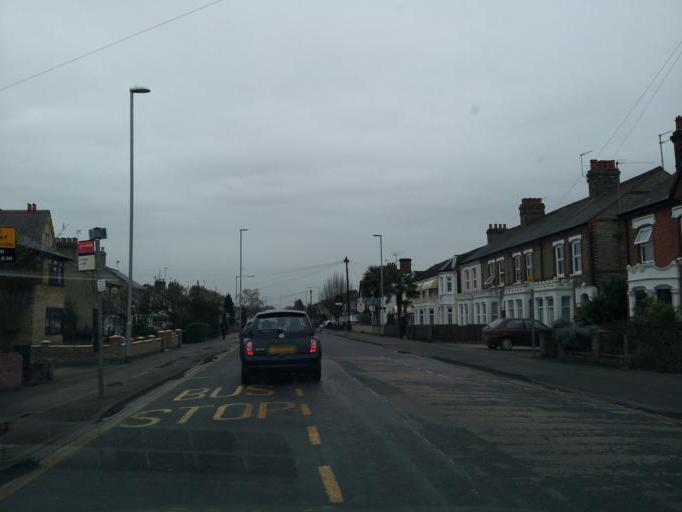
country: GB
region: England
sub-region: Cambridgeshire
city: Cambridge
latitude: 52.1879
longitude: 0.1455
